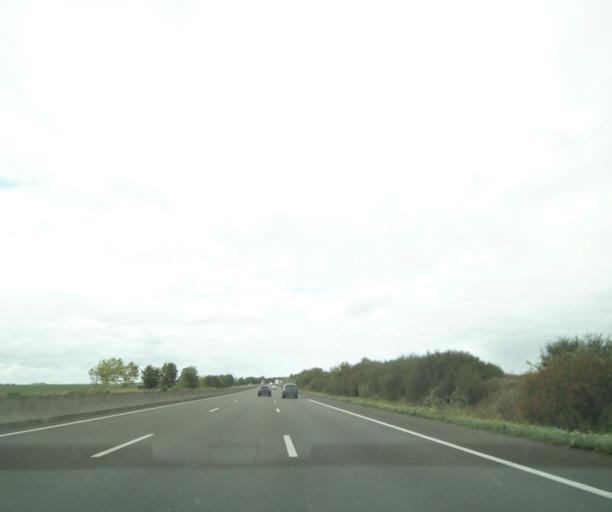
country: FR
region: Ile-de-France
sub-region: Departement de l'Essonne
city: Corbreuse
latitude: 48.4938
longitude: 1.9104
